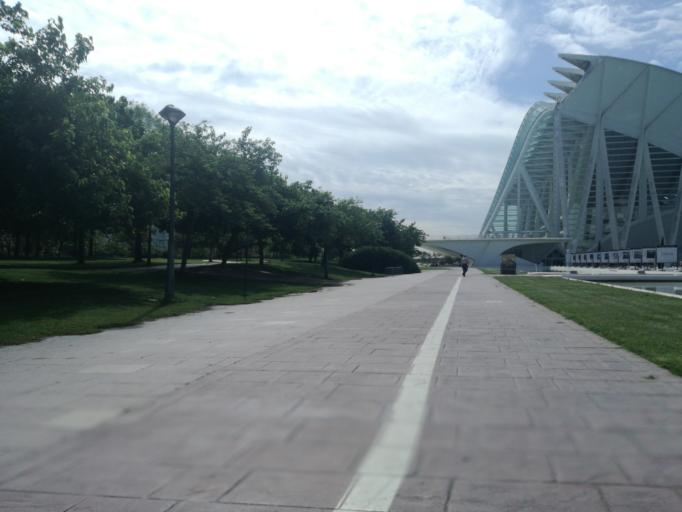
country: ES
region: Valencia
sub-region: Provincia de Valencia
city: Valencia
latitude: 39.4576
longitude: -0.3535
